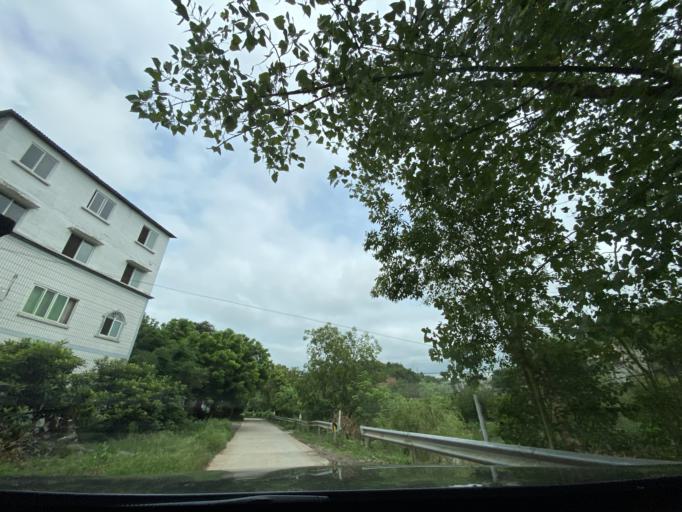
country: CN
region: Sichuan
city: Jiancheng
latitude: 30.3992
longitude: 104.5666
